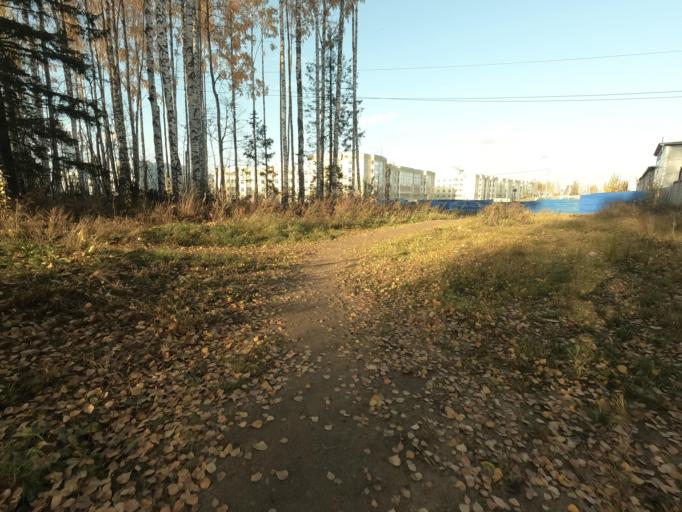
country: RU
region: Leningrad
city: Sertolovo
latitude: 60.1607
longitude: 30.1990
